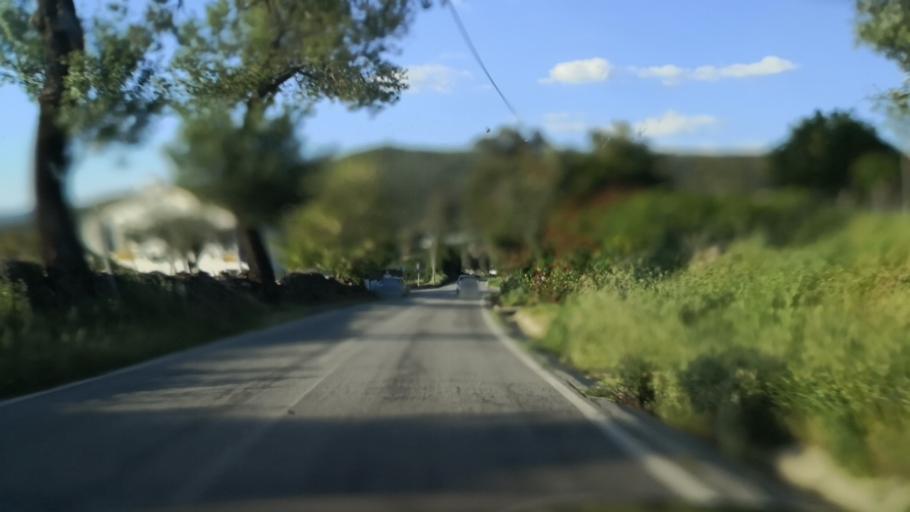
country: PT
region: Portalegre
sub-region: Portalegre
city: Portalegre
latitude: 39.3234
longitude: -7.4365
